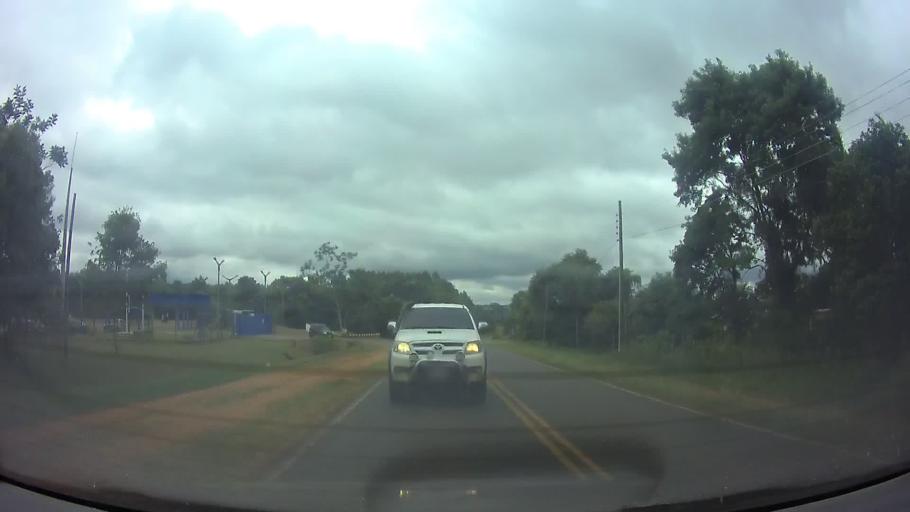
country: PY
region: Central
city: Guarambare
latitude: -25.5119
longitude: -57.4887
